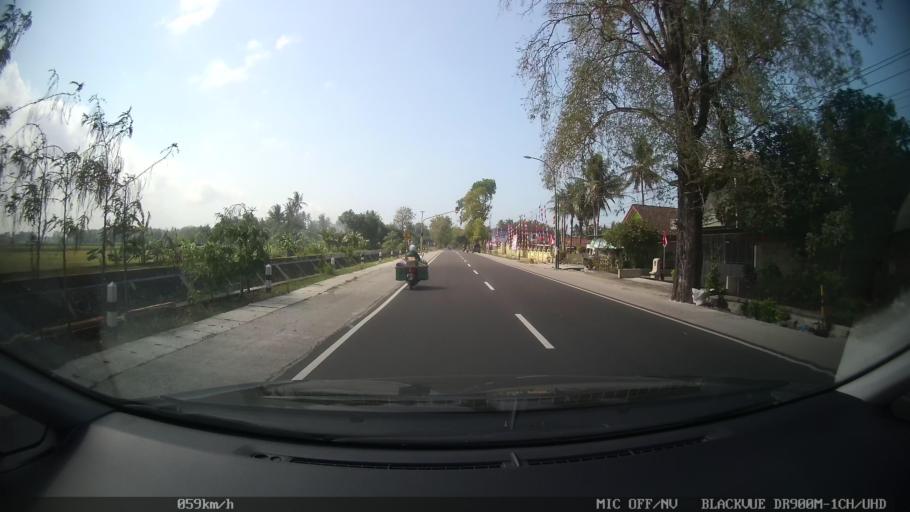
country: ID
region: Daerah Istimewa Yogyakarta
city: Srandakan
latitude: -7.9040
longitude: 110.1692
